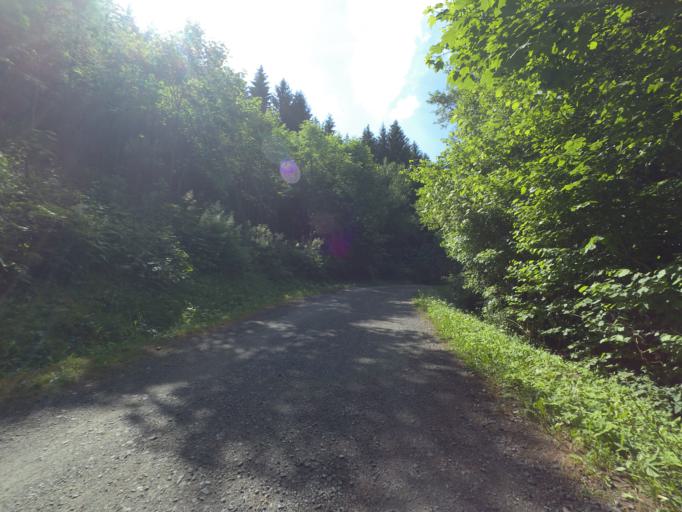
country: AT
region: Carinthia
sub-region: Politischer Bezirk Spittal an der Drau
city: Millstatt
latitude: 46.7744
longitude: 13.6008
